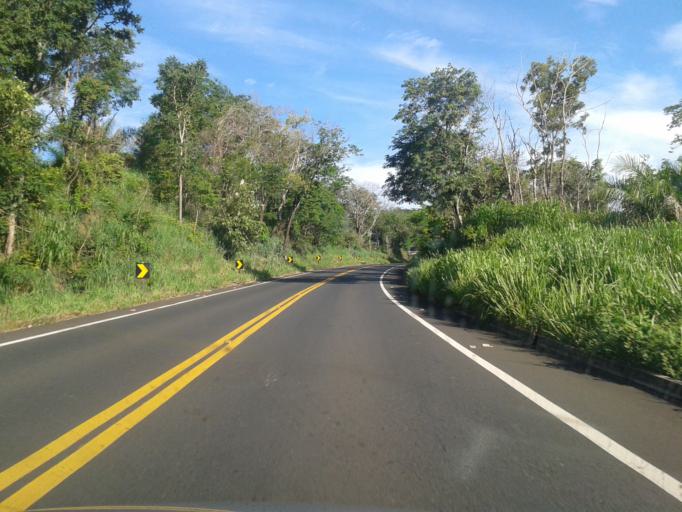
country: BR
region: Goias
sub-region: Caldas Novas
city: Caldas Novas
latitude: -18.1110
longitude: -48.6156
